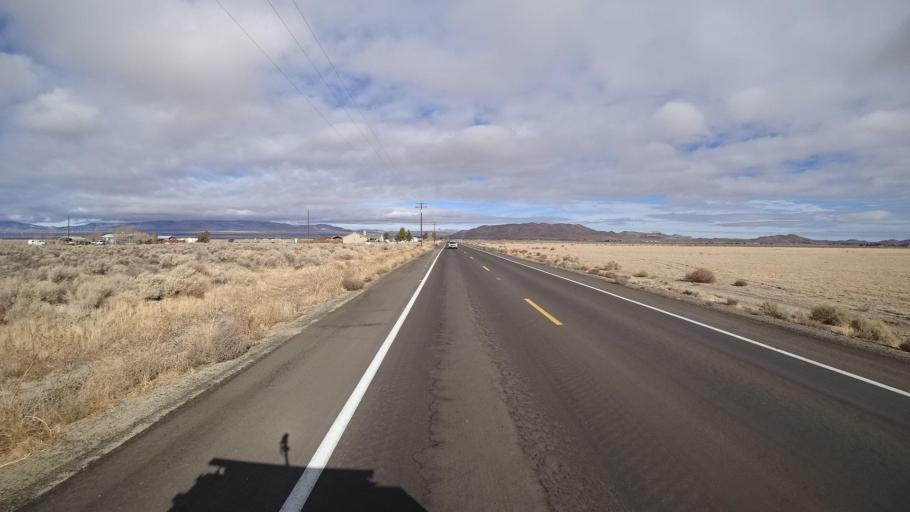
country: US
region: California
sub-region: Kern County
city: Rosamond
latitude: 34.8375
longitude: -118.2908
